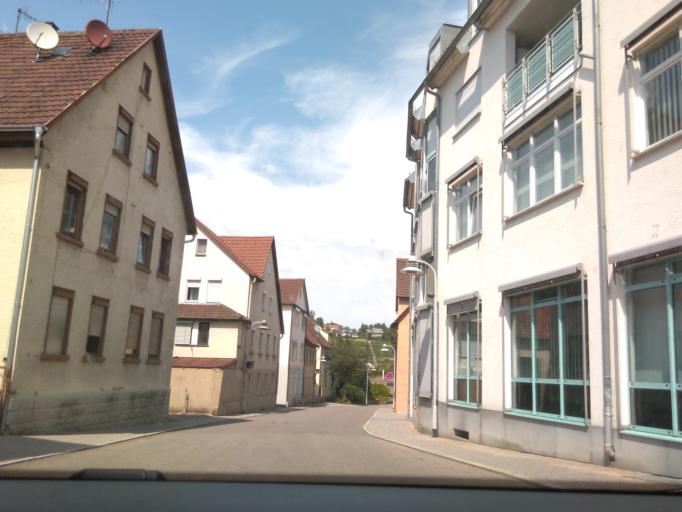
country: DE
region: Baden-Wuerttemberg
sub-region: Regierungsbezirk Stuttgart
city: Lauffen am Neckar
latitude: 49.0761
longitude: 9.1483
